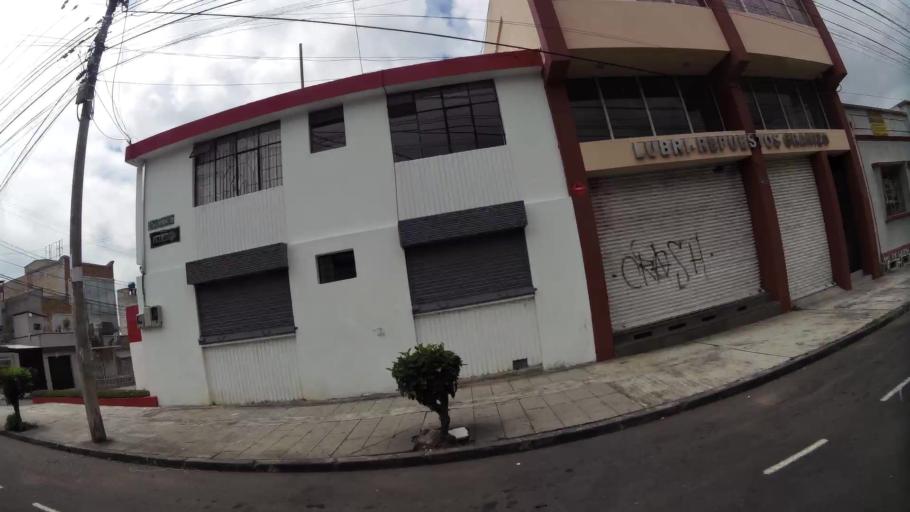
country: EC
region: Pichincha
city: Quito
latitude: -0.1917
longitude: -78.4955
